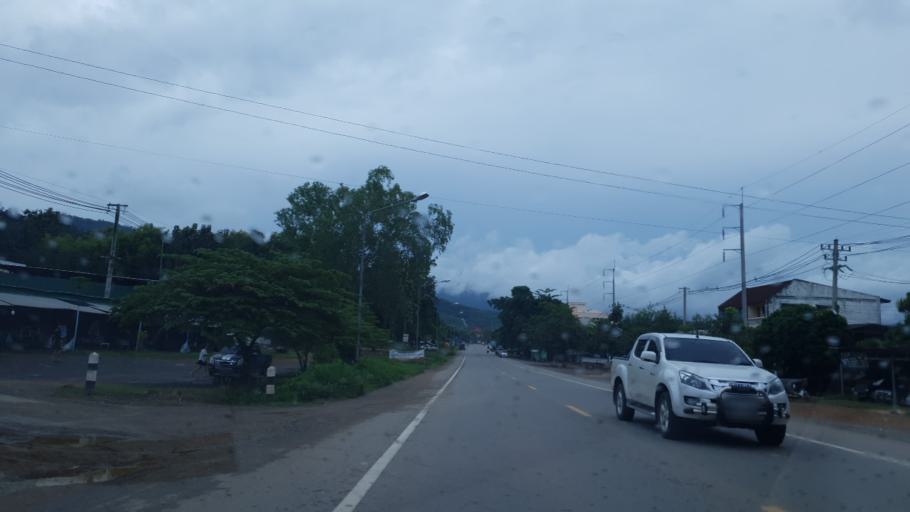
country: TH
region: Mae Hong Son
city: Ban Huai I Huak
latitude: 18.1654
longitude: 97.9377
